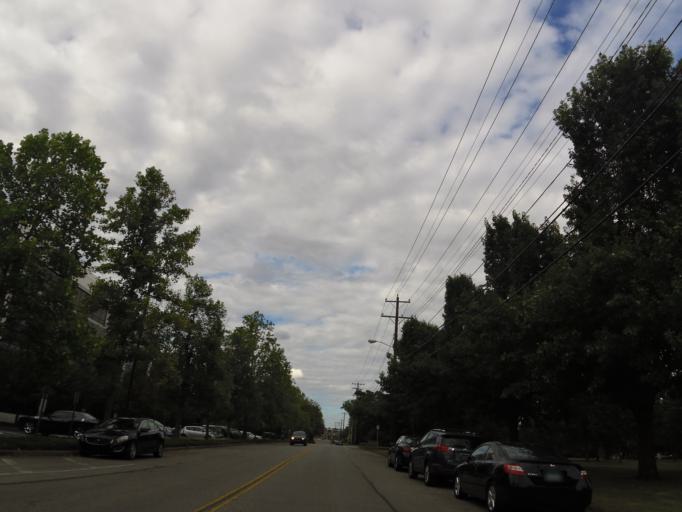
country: US
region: Tennessee
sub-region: Davidson County
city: Nashville
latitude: 36.1520
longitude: -86.8153
